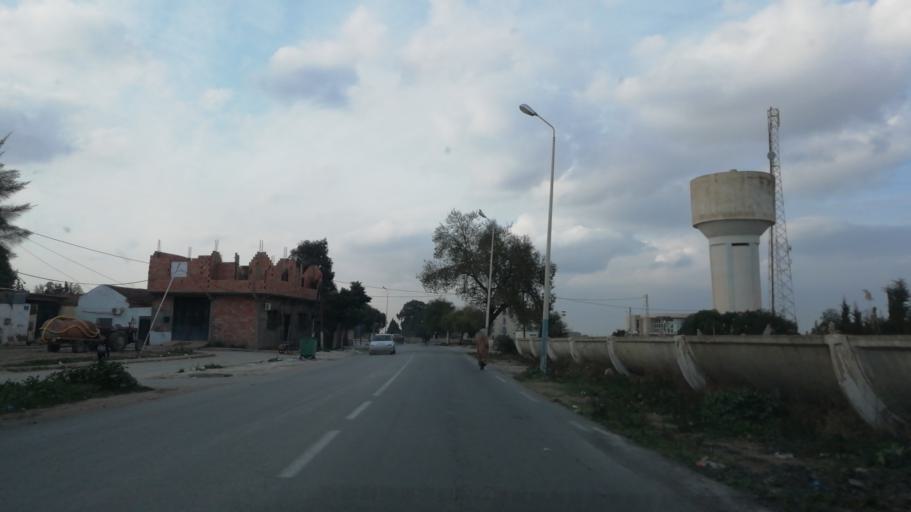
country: DZ
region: Mascara
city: Sig
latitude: 35.6553
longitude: 0.0164
